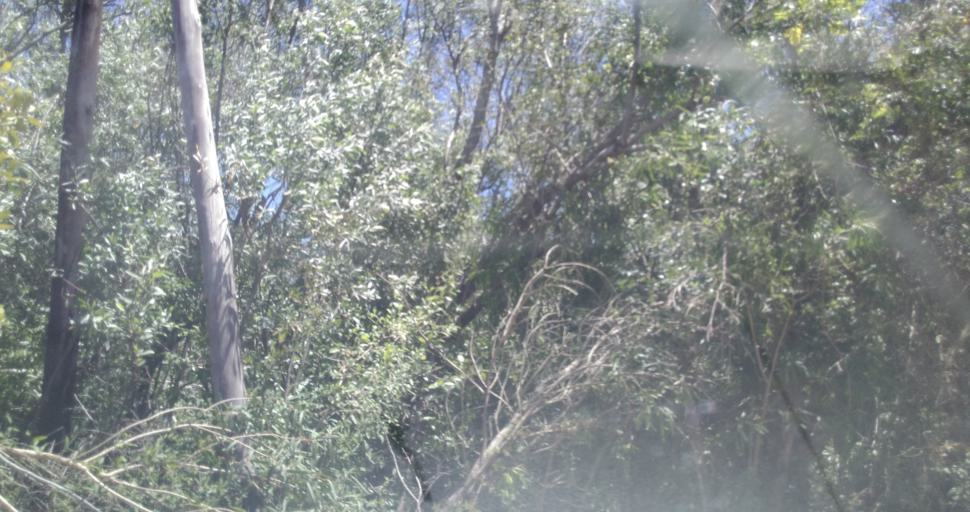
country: AR
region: Chaco
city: Fontana
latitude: -27.4106
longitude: -59.0138
